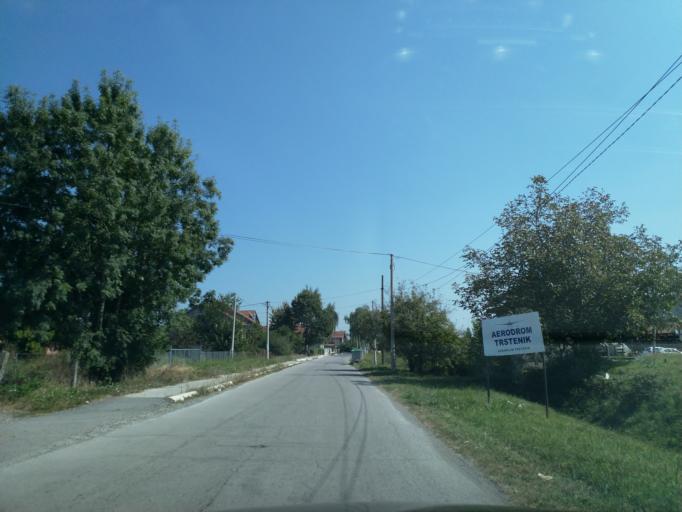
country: RS
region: Central Serbia
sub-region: Rasinski Okrug
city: Trstenik
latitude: 43.6143
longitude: 21.0160
